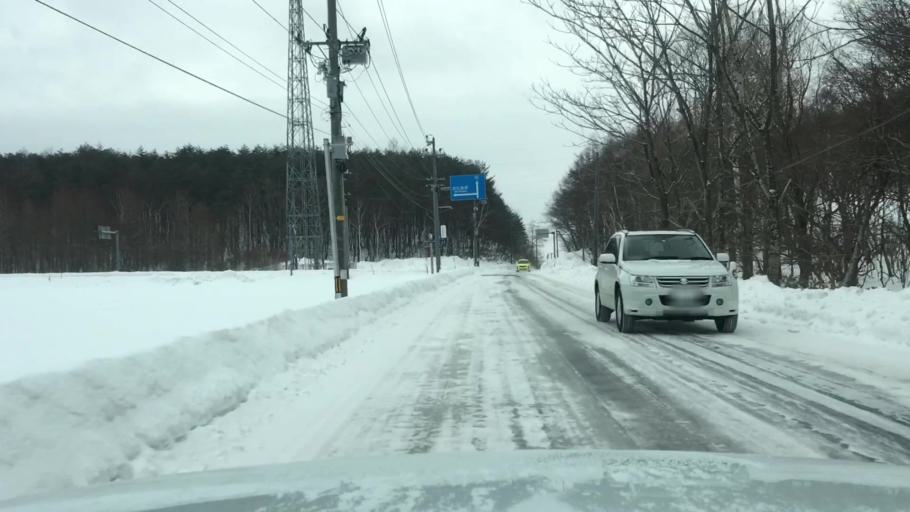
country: JP
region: Iwate
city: Shizukuishi
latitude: 39.9712
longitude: 141.0012
